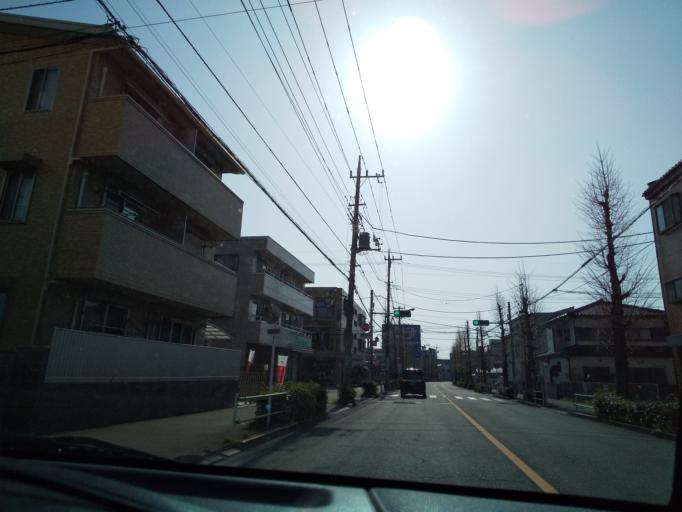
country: JP
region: Tokyo
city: Fussa
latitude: 35.7107
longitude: 139.3659
